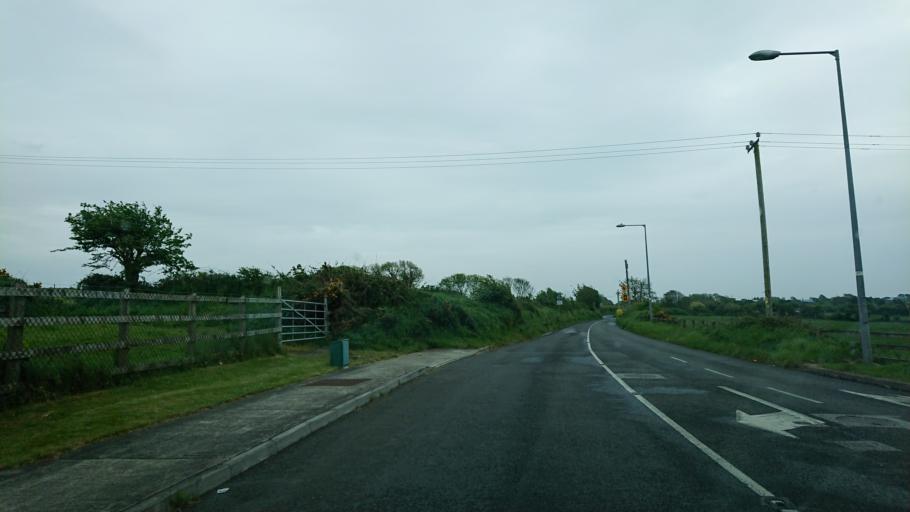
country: IE
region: Munster
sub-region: Waterford
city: Waterford
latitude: 52.2289
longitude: -7.0610
